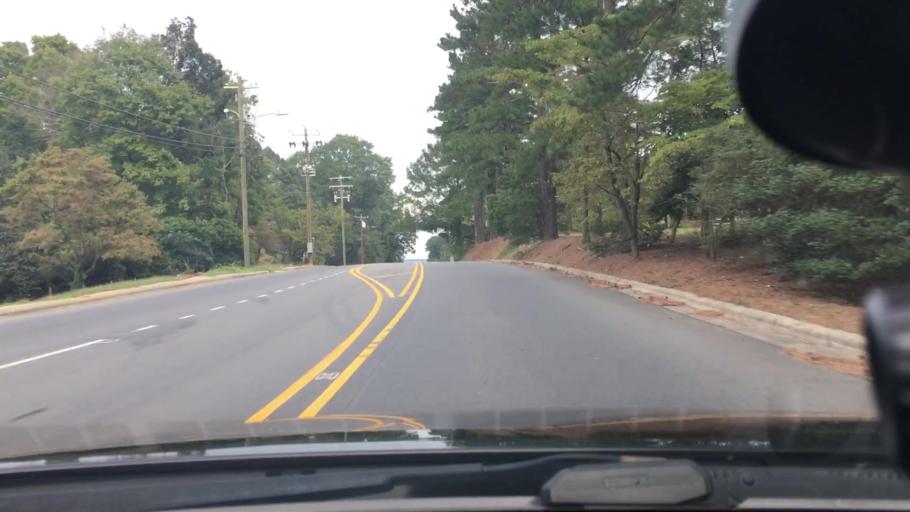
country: US
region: North Carolina
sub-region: Montgomery County
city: Troy
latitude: 35.3588
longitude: -79.8864
